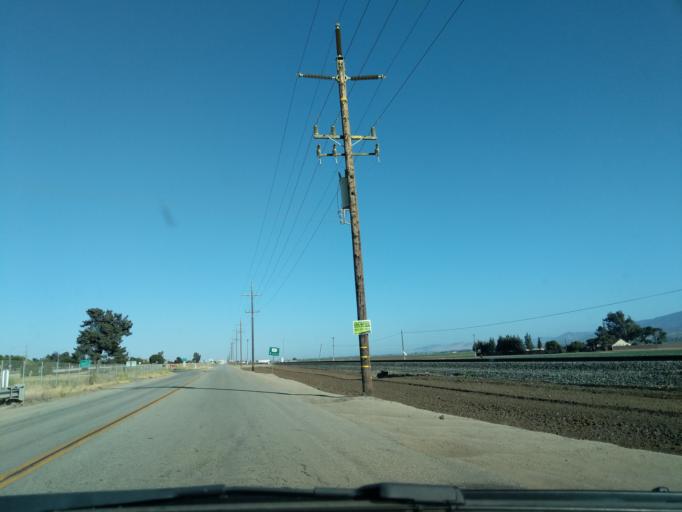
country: US
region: California
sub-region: Monterey County
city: Gonzales
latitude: 36.4644
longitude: -121.3879
